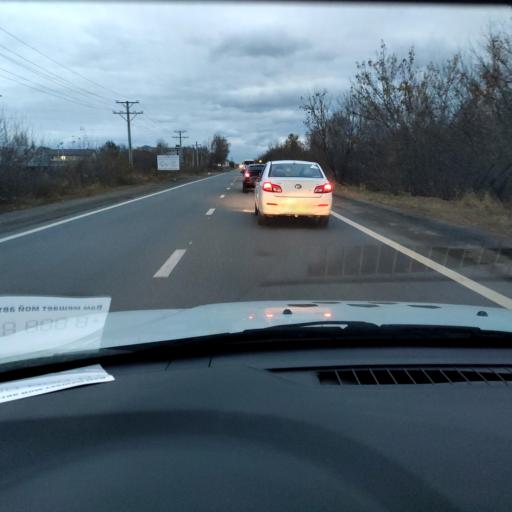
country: RU
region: Samara
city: Tol'yatti
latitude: 53.5551
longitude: 49.3662
